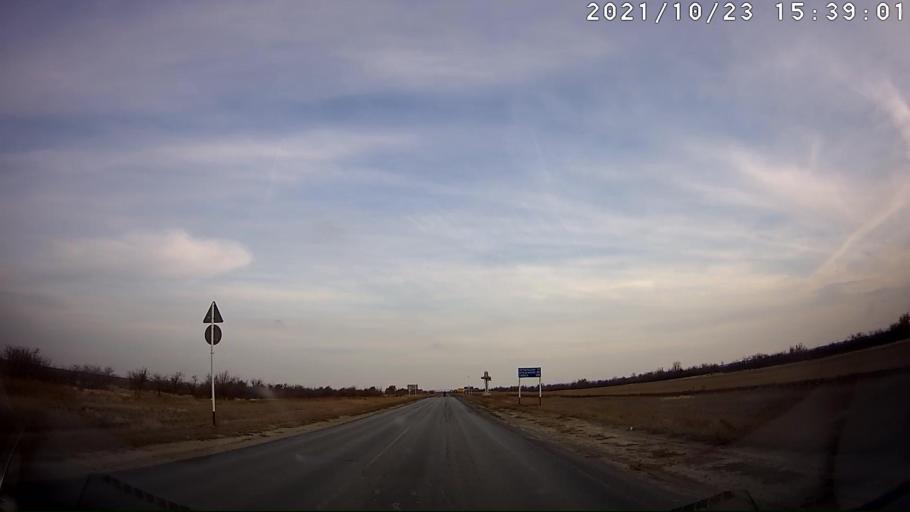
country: RU
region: Volgograd
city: Bereslavka
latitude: 48.1283
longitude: 44.1221
